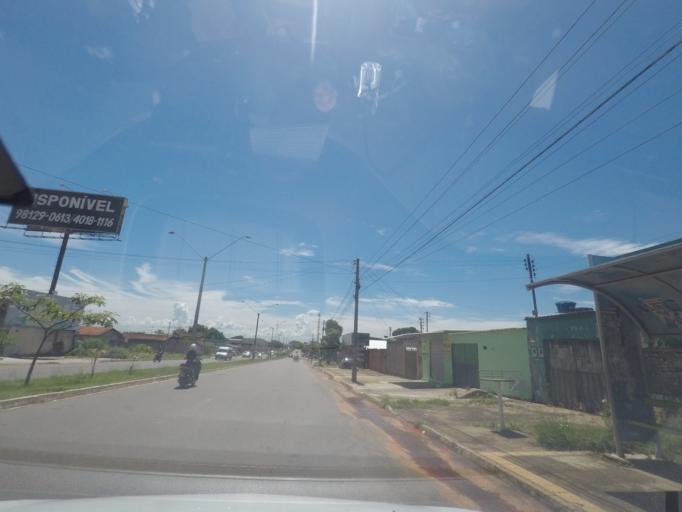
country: BR
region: Goias
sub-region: Aparecida De Goiania
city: Aparecida de Goiania
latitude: -16.7716
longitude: -49.3316
